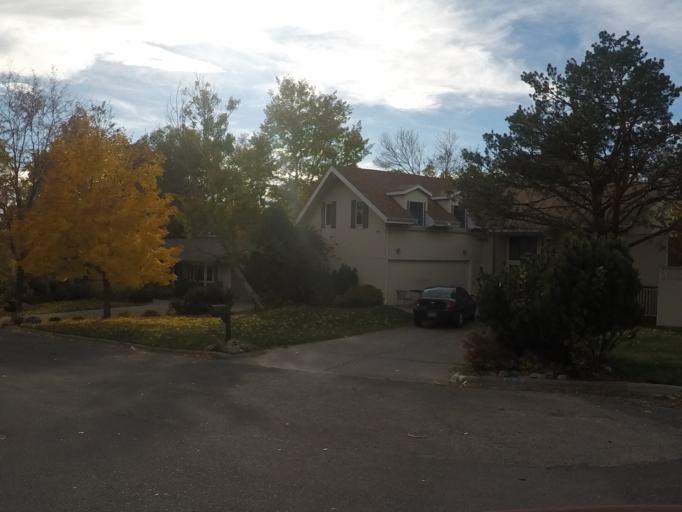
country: US
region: Montana
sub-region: Yellowstone County
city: Billings
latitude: 45.8008
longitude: -108.5590
